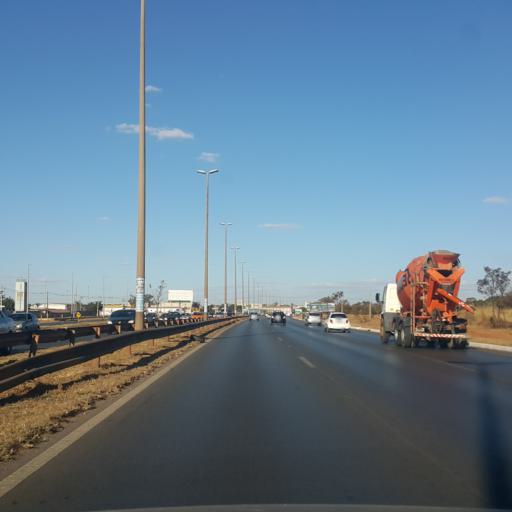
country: BR
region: Federal District
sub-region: Brasilia
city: Brasilia
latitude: -15.7868
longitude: -47.9927
